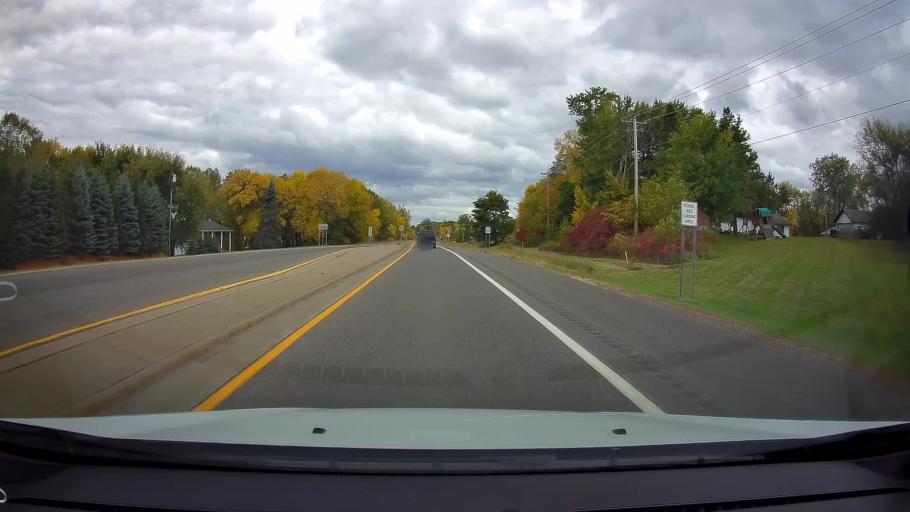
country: US
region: Minnesota
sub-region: Chisago County
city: Chisago City
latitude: 45.3689
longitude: -92.8999
